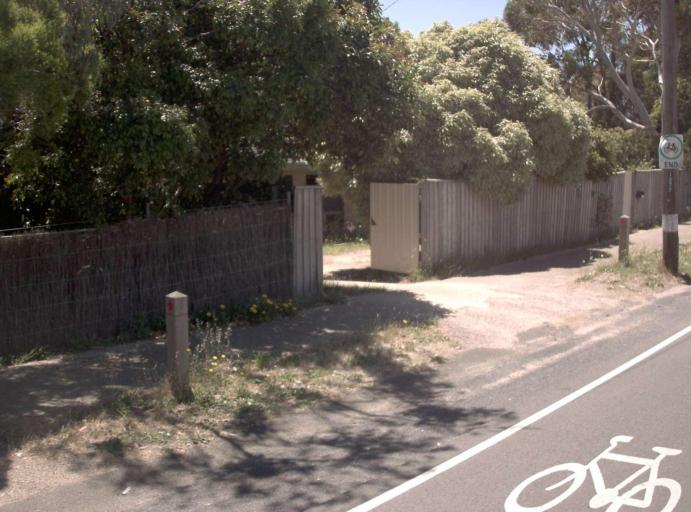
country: AU
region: Victoria
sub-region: Mornington Peninsula
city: Mount Eliza
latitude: -38.2014
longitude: 145.0809
